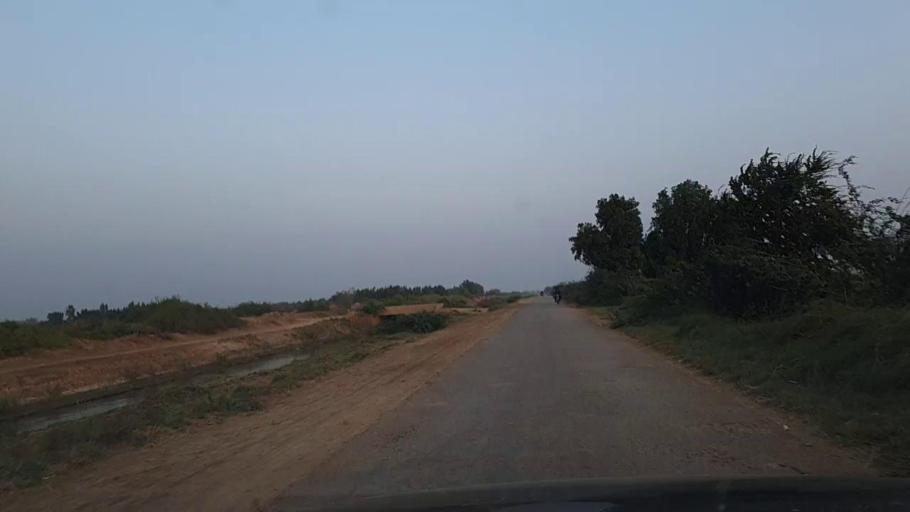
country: PK
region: Sindh
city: Mirpur Sakro
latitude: 24.6335
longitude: 67.6180
